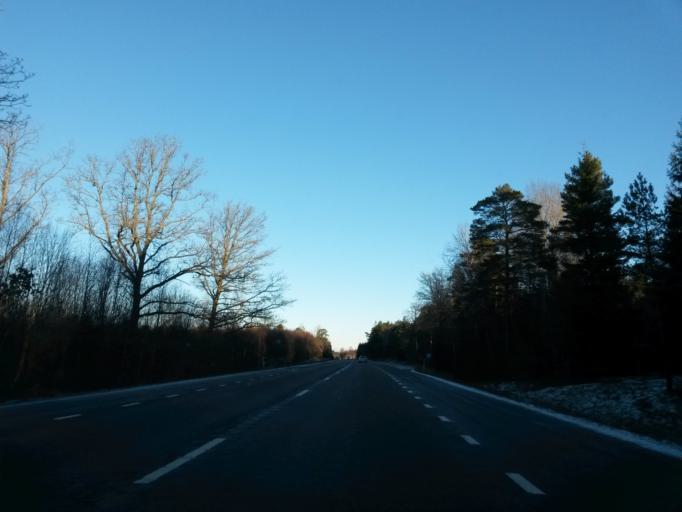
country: SE
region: Vaestra Goetaland
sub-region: Vargarda Kommun
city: Vargarda
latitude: 58.1217
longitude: 12.8502
